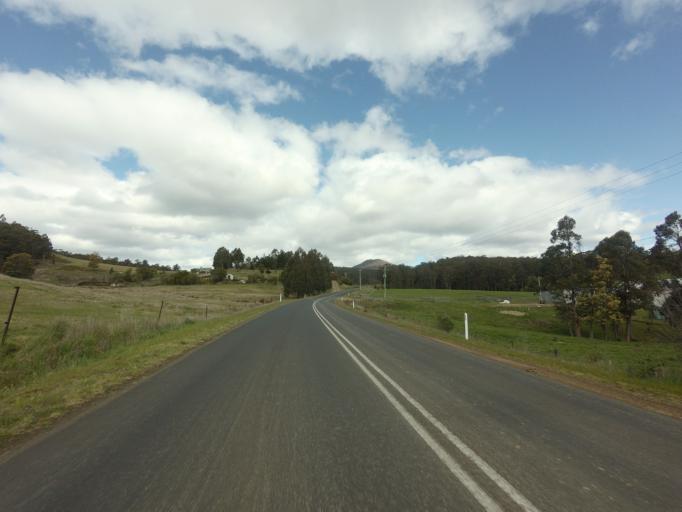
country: AU
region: Tasmania
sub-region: Huon Valley
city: Geeveston
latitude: -43.1918
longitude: 146.9380
